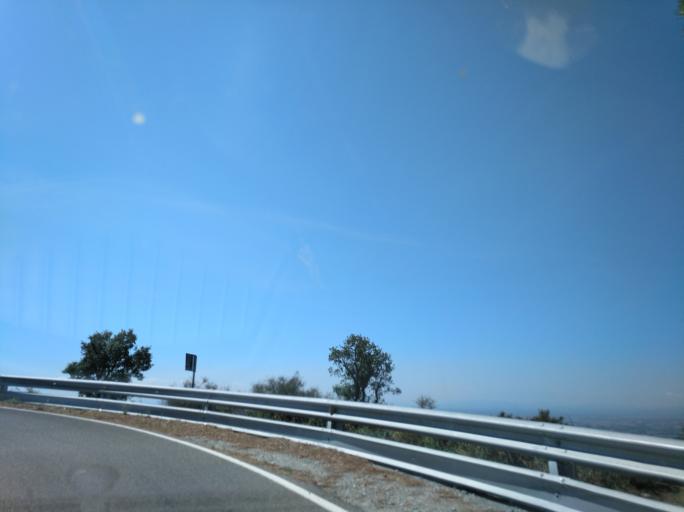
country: ES
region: Catalonia
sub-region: Provincia de Girona
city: Pau
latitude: 42.3297
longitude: 3.1354
